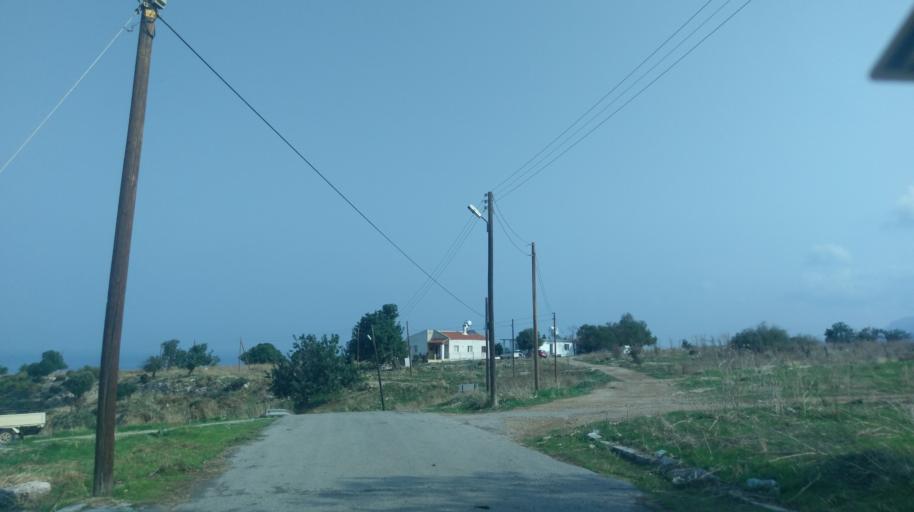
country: CY
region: Keryneia
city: Kyrenia
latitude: 35.3092
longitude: 33.4688
